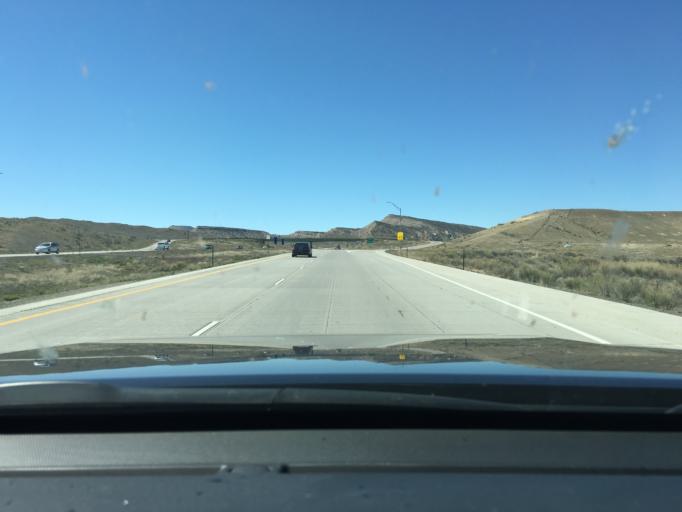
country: US
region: Colorado
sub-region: Mesa County
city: Loma
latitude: 39.1780
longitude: -108.8082
